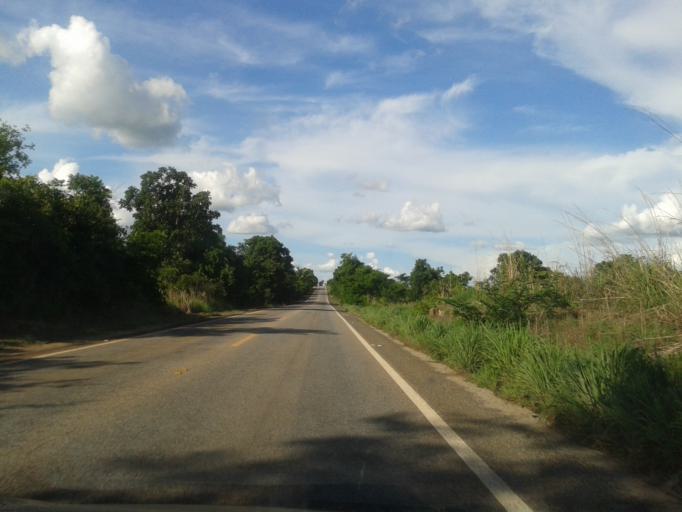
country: BR
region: Goias
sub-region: Mozarlandia
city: Mozarlandia
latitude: -14.5408
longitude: -50.4897
